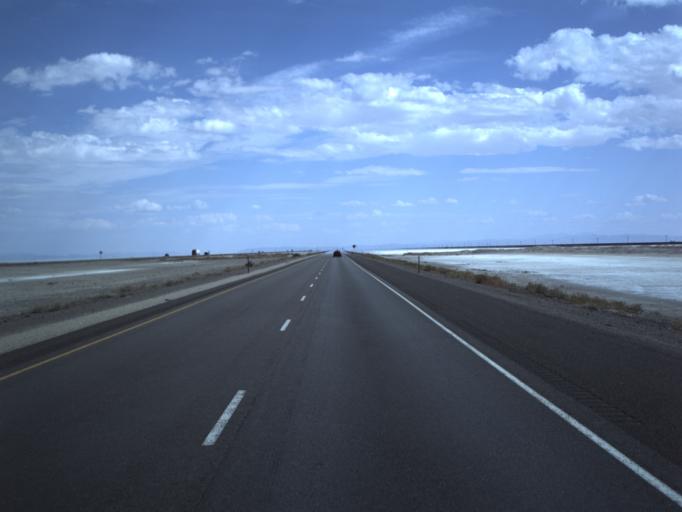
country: US
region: Utah
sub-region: Tooele County
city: Wendover
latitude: 40.7373
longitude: -113.7938
